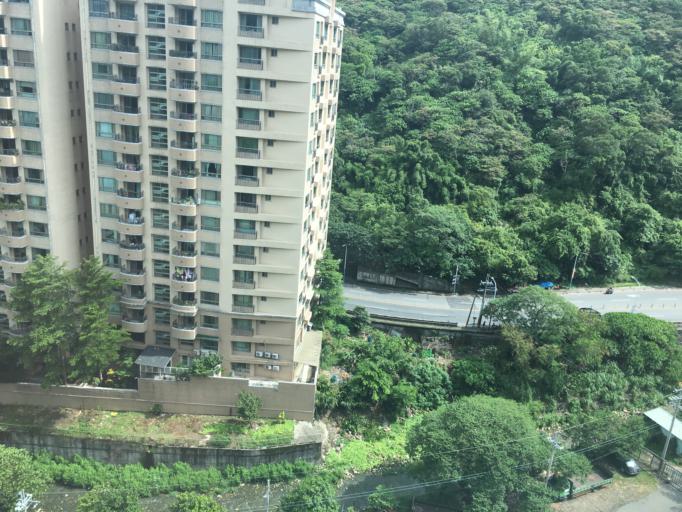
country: TW
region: Taipei
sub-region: Taipei
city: Banqiao
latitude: 25.0288
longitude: 121.4081
